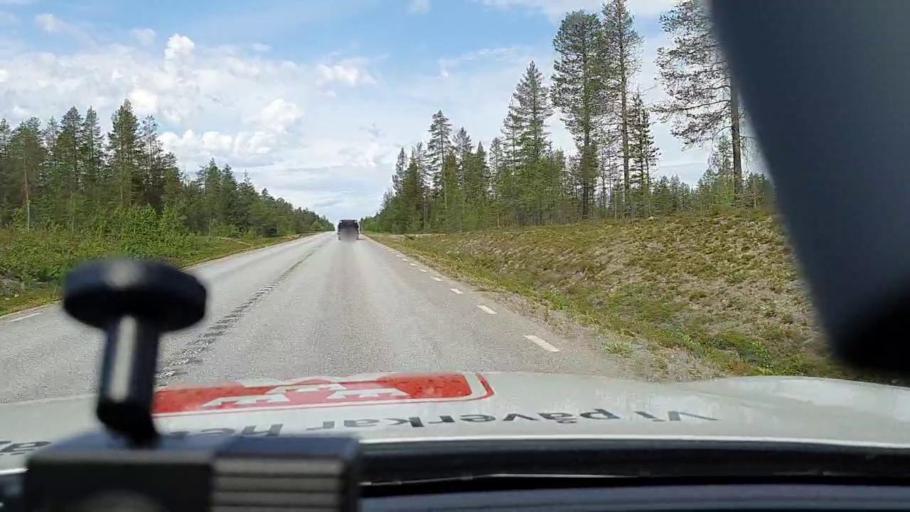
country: SE
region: Norrbotten
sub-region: Jokkmokks Kommun
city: Jokkmokk
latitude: 66.5240
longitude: 20.2024
